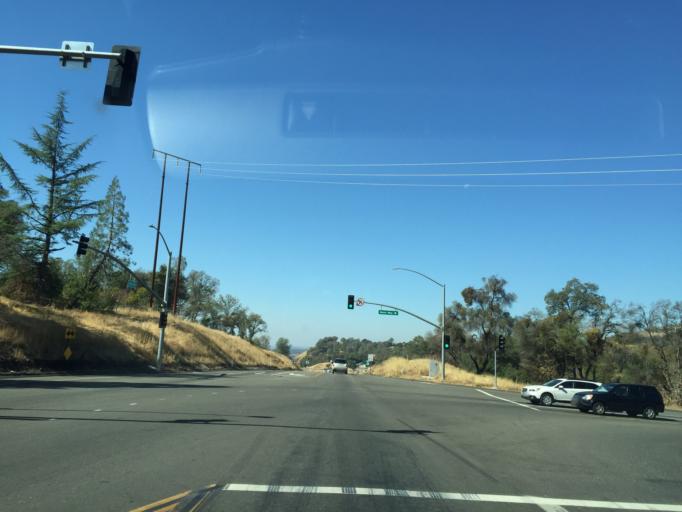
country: US
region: California
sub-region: Tuolumne County
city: Mono Vista
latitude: 37.9821
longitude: -120.2977
